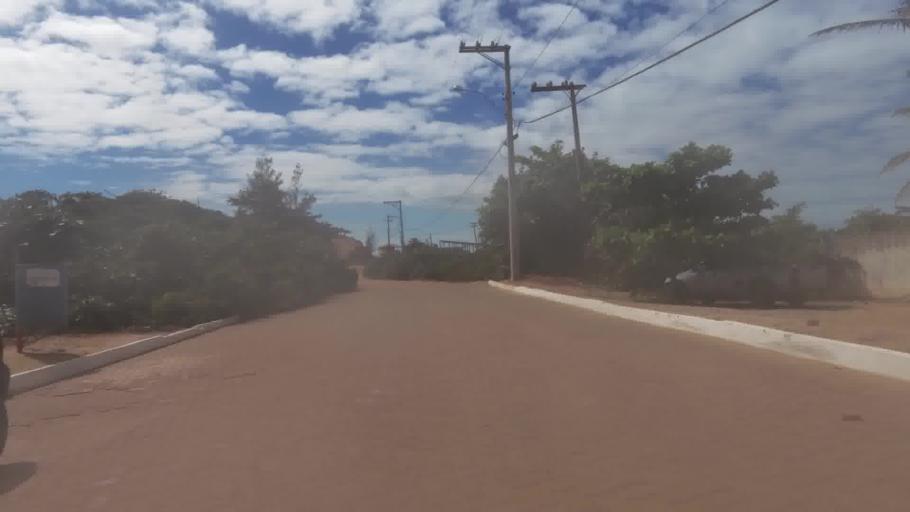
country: BR
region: Espirito Santo
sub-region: Marataizes
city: Marataizes
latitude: -21.1901
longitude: -40.9283
